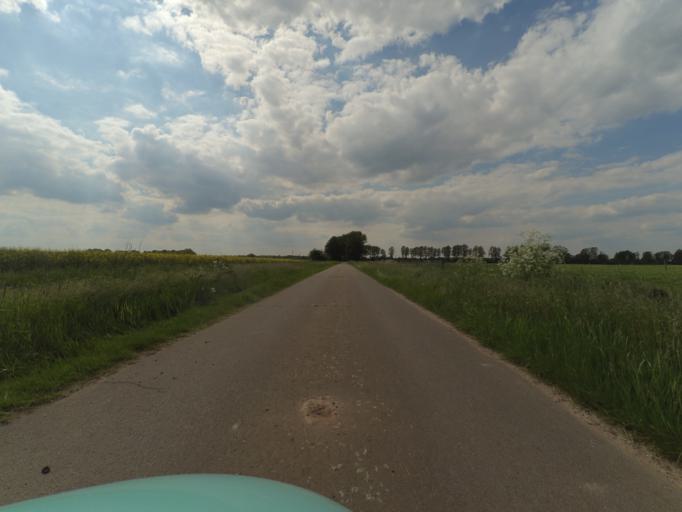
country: DE
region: Lower Saxony
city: Haenigsen
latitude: 52.5129
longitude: 10.0786
